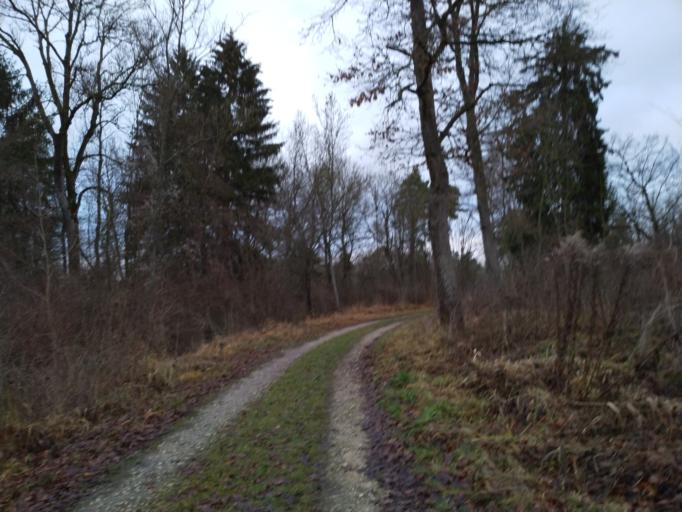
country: DE
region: Bavaria
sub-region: Swabia
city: Guenzburg
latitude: 48.4695
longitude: 10.3023
